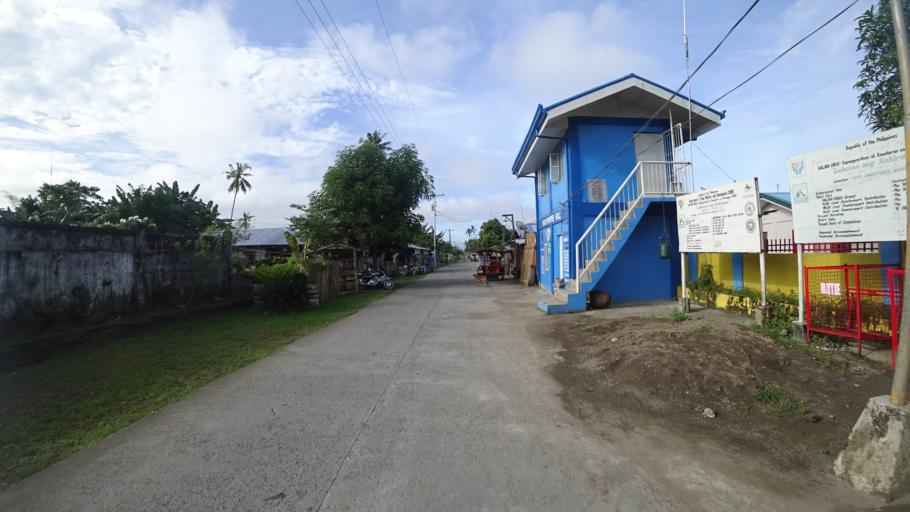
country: PH
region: Eastern Visayas
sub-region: Province of Leyte
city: Alangalang
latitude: 11.1804
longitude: 124.8716
